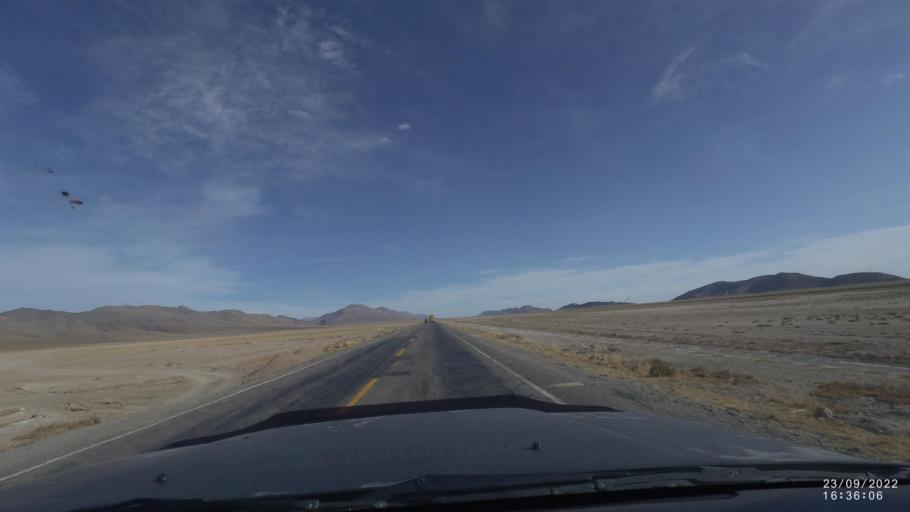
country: BO
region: Oruro
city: Machacamarca
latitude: -18.2147
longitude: -67.0090
